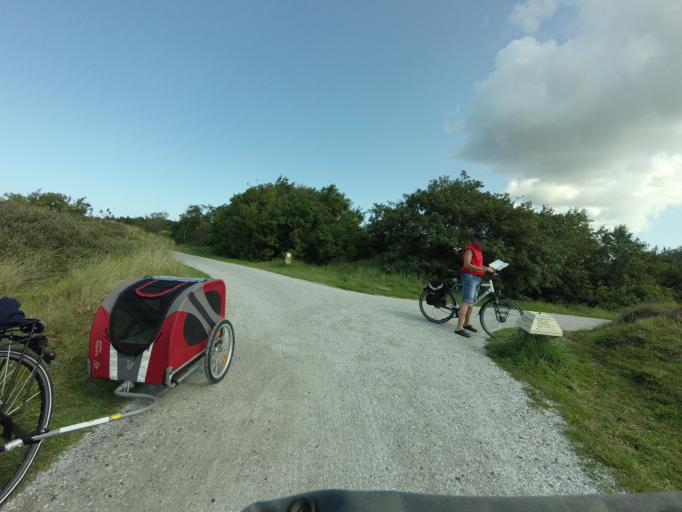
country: NL
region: Friesland
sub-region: Gemeente Terschelling
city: West-Terschelling
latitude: 53.3680
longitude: 5.2029
